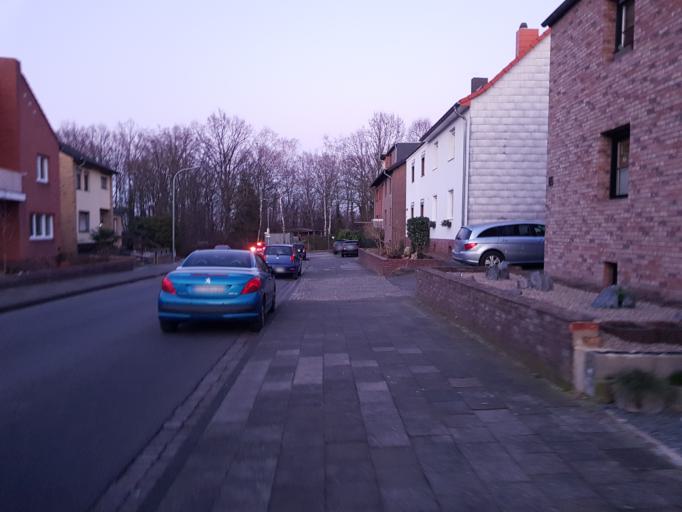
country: DE
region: North Rhine-Westphalia
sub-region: Regierungsbezirk Koln
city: Langerwehe
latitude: 50.8221
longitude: 6.3222
